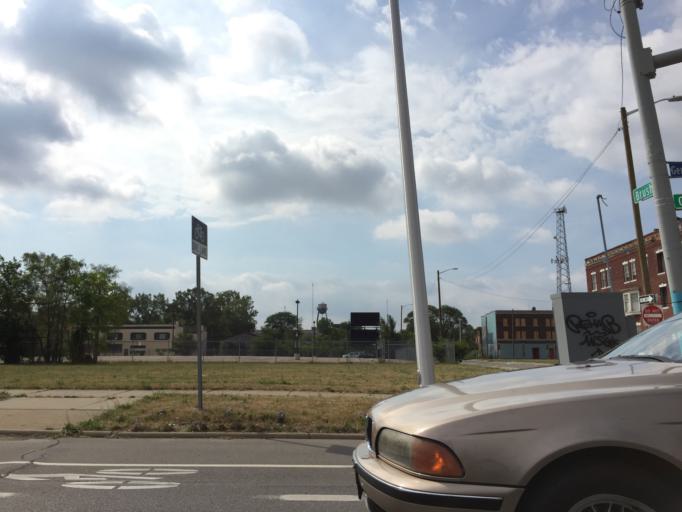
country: US
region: Michigan
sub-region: Wayne County
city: Hamtramck
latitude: 42.3719
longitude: -83.0685
